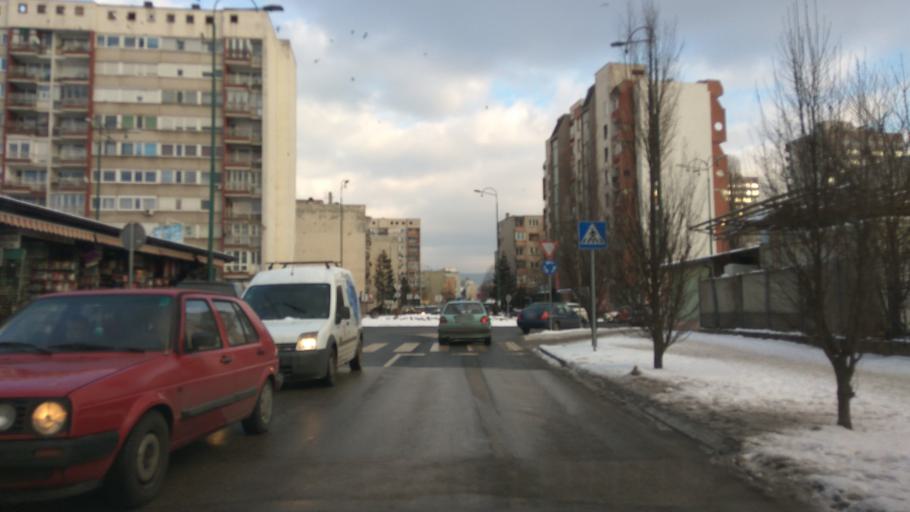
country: BA
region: Federation of Bosnia and Herzegovina
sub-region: Kanton Sarajevo
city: Sarajevo
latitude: 43.8508
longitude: 18.3657
